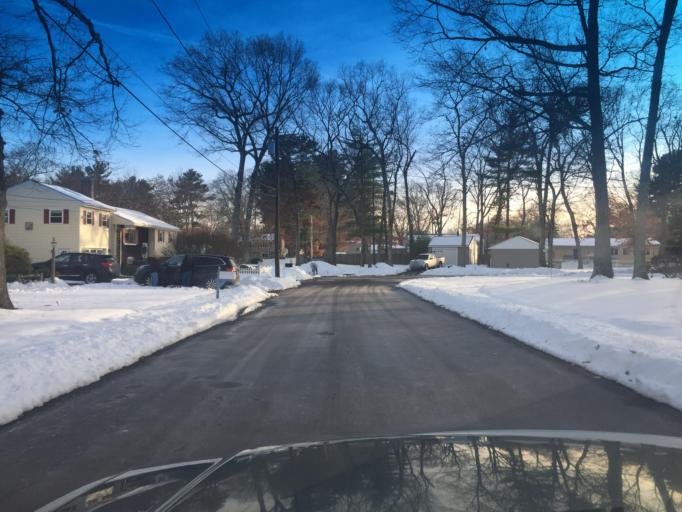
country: US
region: Massachusetts
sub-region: Norfolk County
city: Bellingham
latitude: 42.1103
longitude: -71.4812
